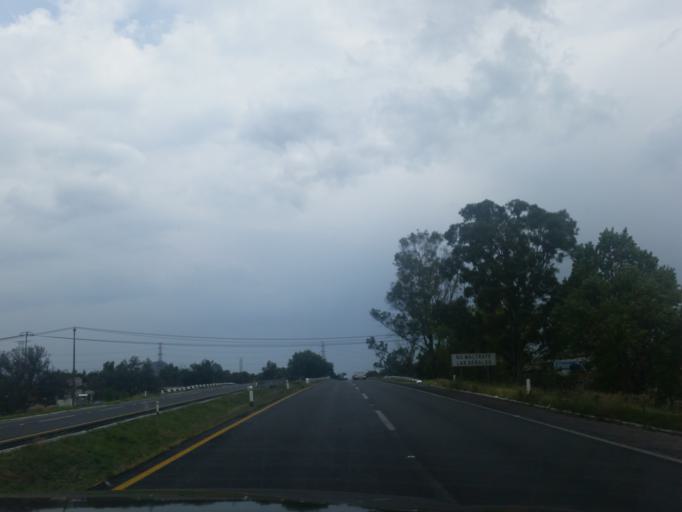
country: MX
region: Morelos
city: Teotihuacan de Arista
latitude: 19.6680
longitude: -98.8691
